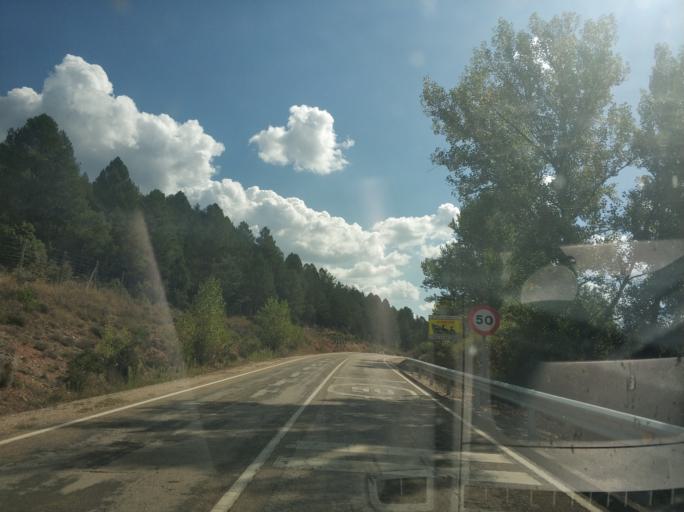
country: ES
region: Castille and Leon
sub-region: Provincia de Soria
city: San Leonardo de Yague
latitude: 41.8211
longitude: -3.0701
